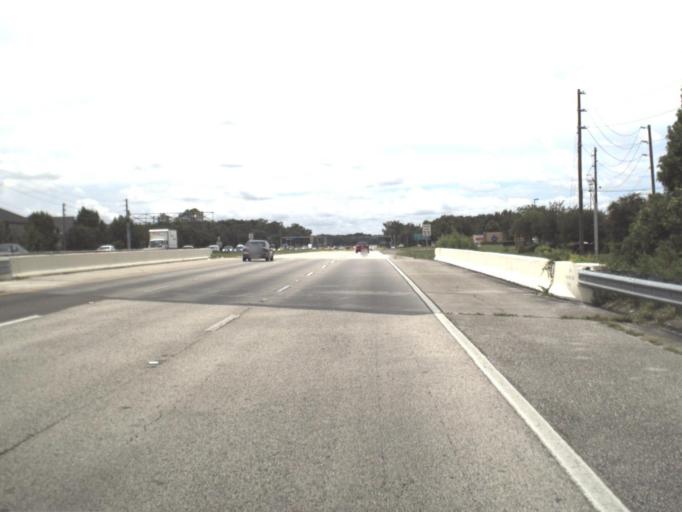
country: US
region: Florida
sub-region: Hillsborough County
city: Pebble Creek
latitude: 28.1860
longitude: -82.3553
